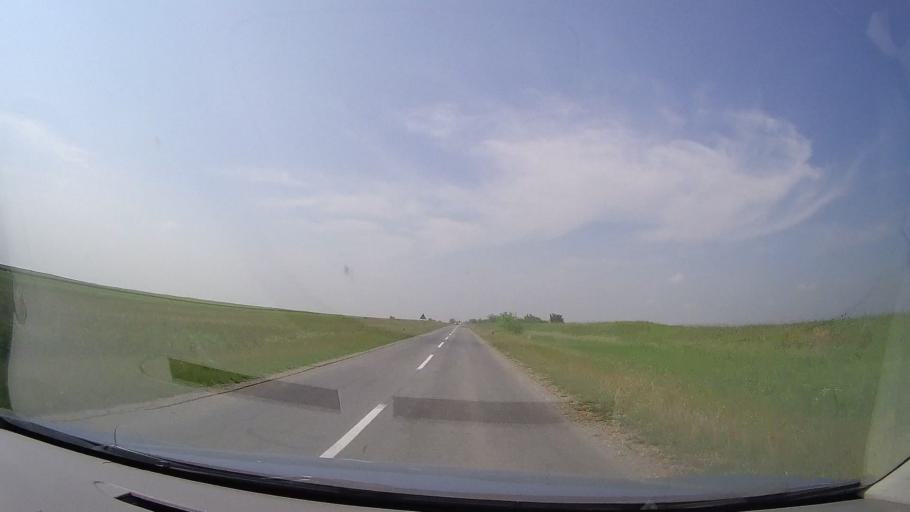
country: RS
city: Samos
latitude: 45.1850
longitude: 20.7631
